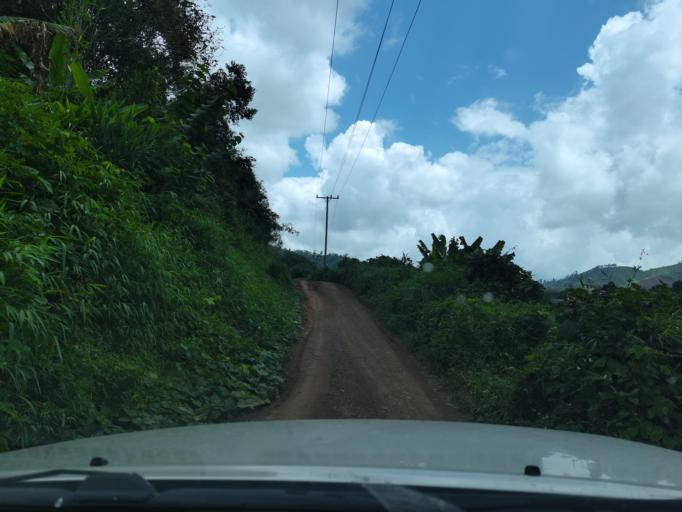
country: LA
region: Loungnamtha
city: Muang Long
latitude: 20.7525
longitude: 101.0181
